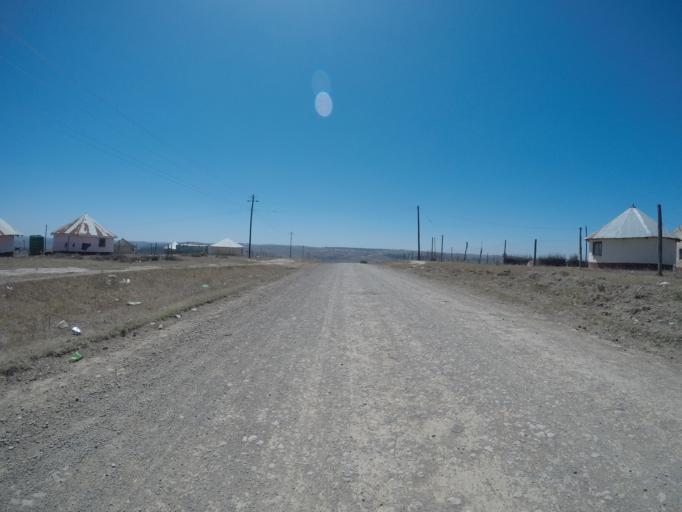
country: ZA
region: Eastern Cape
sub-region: OR Tambo District Municipality
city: Mthatha
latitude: -31.8826
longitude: 28.8749
